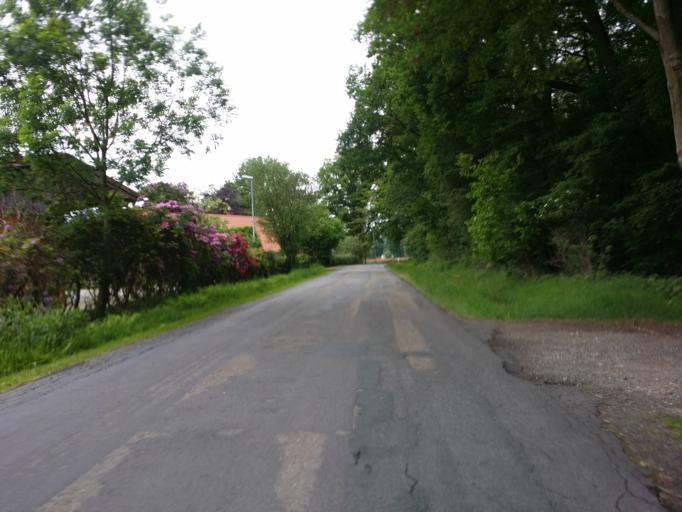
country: DE
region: Lower Saxony
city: Rastede
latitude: 53.2366
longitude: 8.2121
